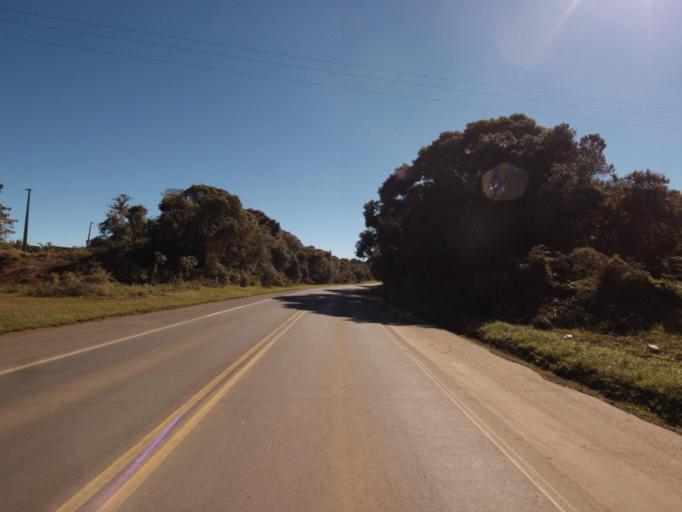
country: BR
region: Santa Catarina
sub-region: Xanxere
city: Xanxere
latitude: -26.8763
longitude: -52.1923
